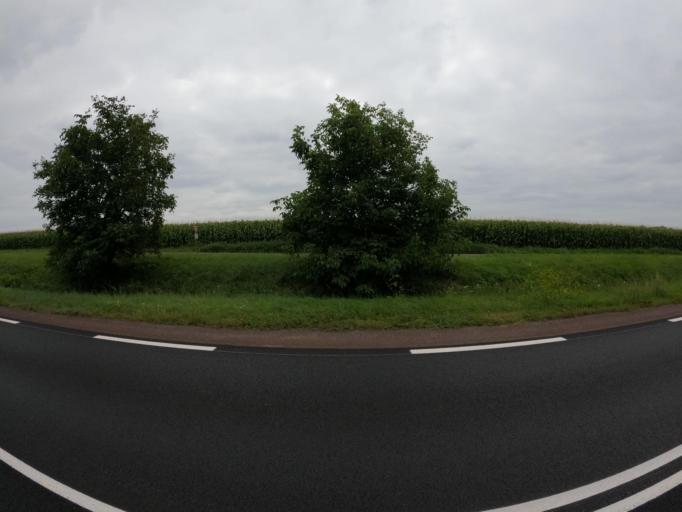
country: FR
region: Pays de la Loire
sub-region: Departement de la Vendee
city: Benet
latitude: 46.3965
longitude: -0.6533
